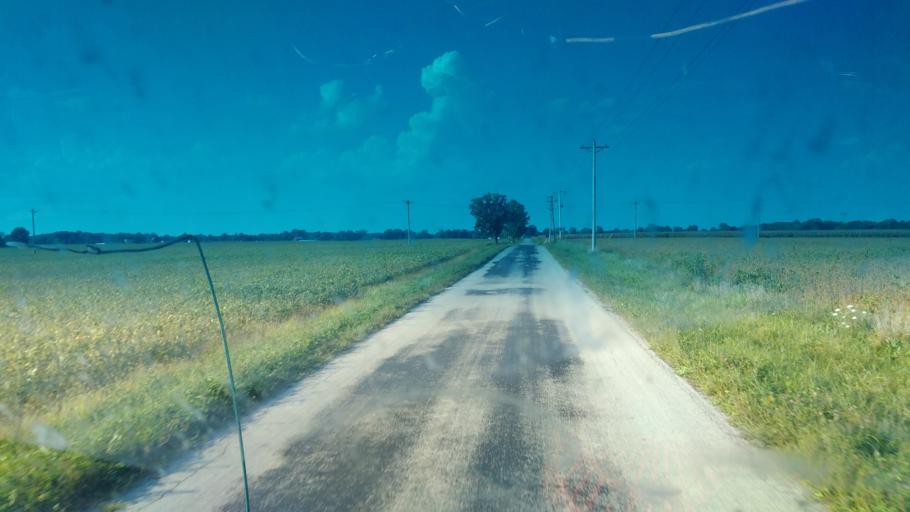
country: US
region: Ohio
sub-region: Wyandot County
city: Upper Sandusky
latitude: 40.9193
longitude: -83.1893
